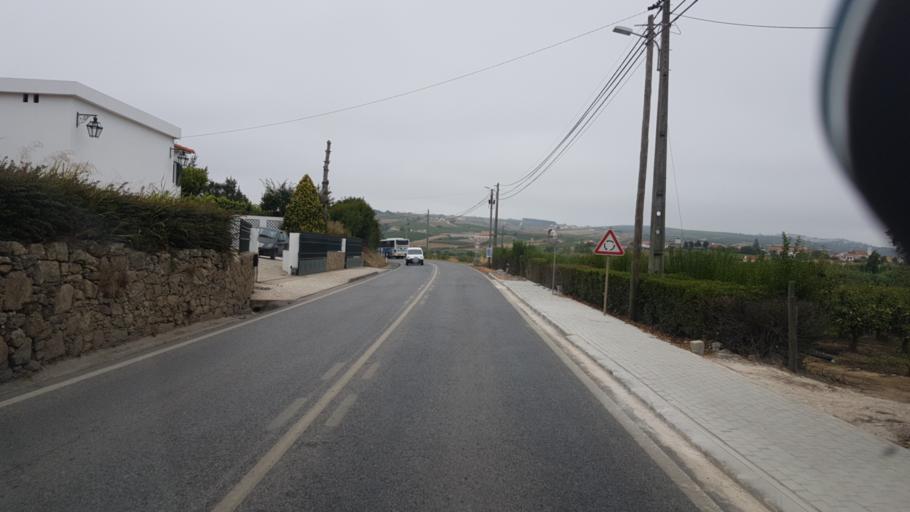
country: PT
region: Lisbon
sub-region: Torres Vedras
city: Torres Vedras
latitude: 39.0880
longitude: -9.3108
